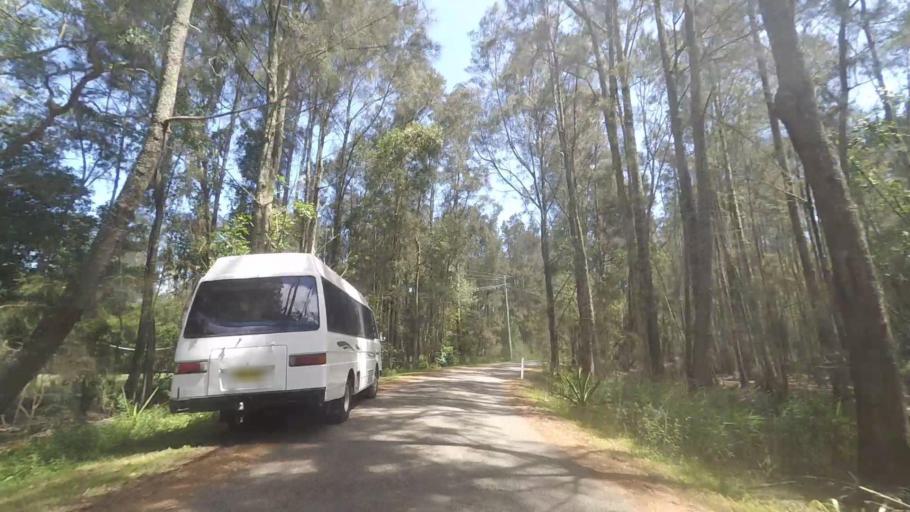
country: AU
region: New South Wales
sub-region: Great Lakes
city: Bulahdelah
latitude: -32.5058
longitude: 152.3035
